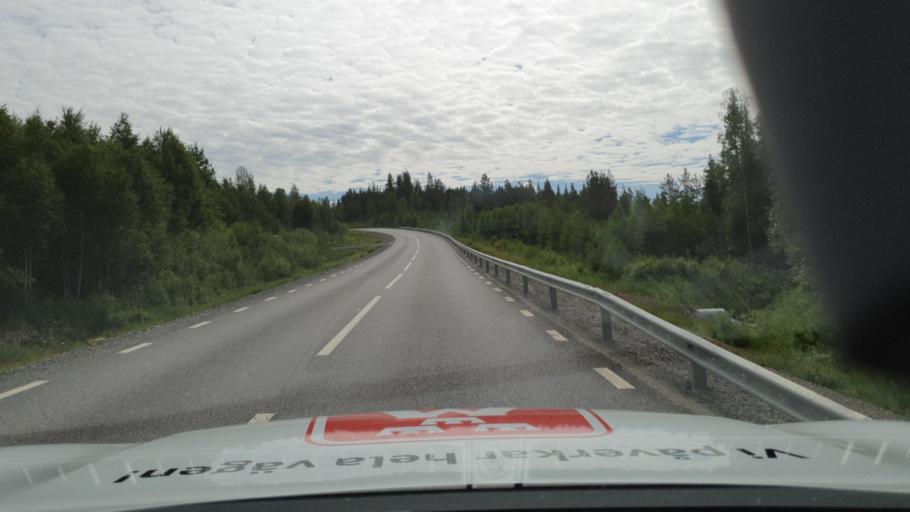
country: SE
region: Vaesterbotten
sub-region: Vindelns Kommun
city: Vindeln
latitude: 64.2532
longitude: 19.9664
